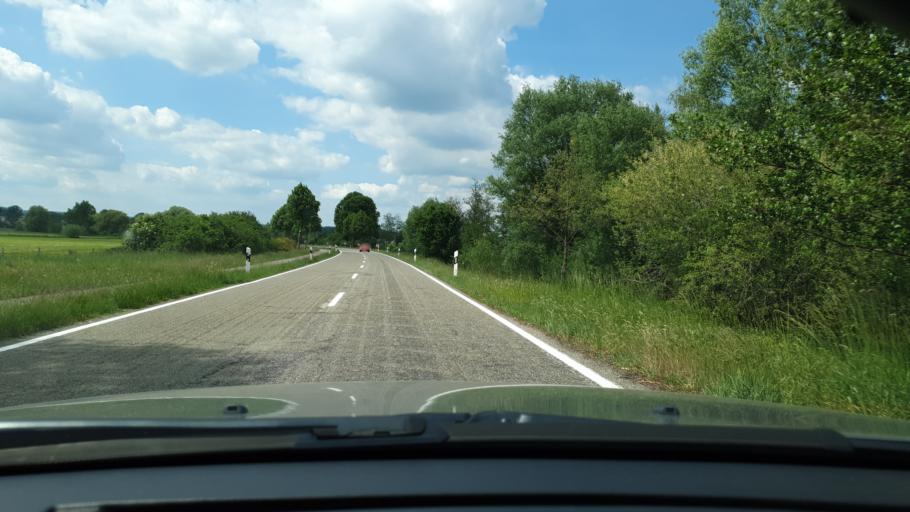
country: DE
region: Rheinland-Pfalz
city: Hutschenhausen
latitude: 49.4108
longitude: 7.4880
